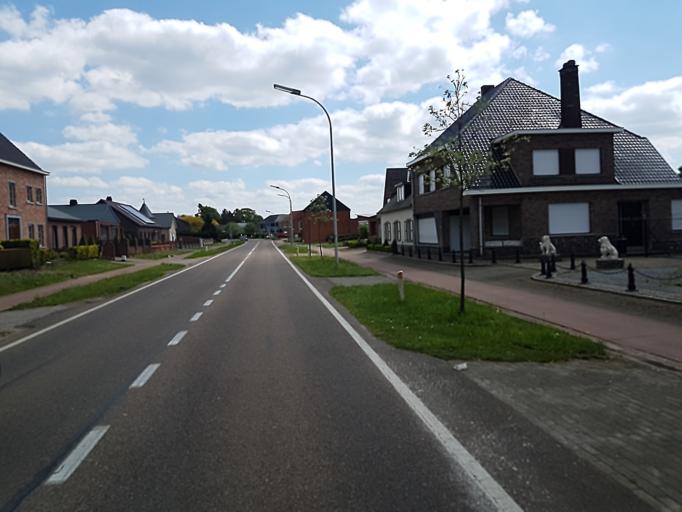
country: BE
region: Flanders
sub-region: Provincie Antwerpen
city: Laakdal
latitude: 51.0672
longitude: 4.9716
